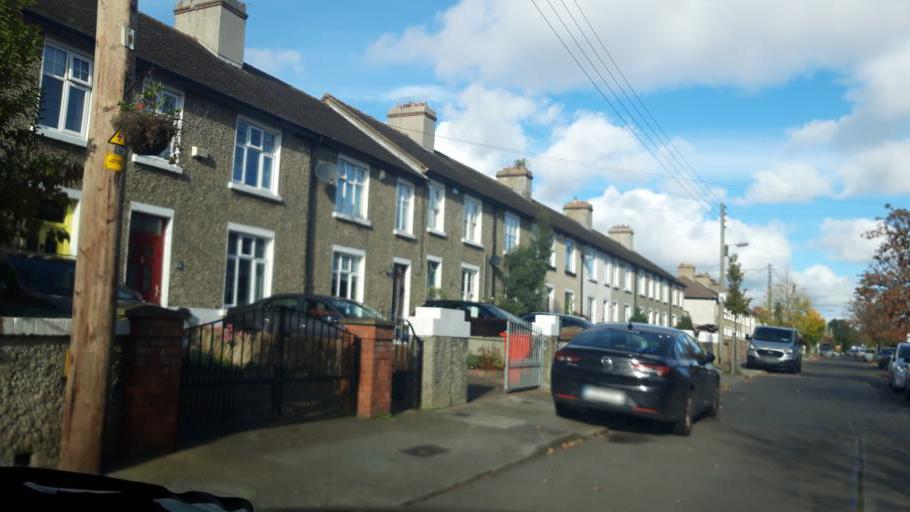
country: IE
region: Leinster
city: Marino
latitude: 53.3751
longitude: -6.2261
